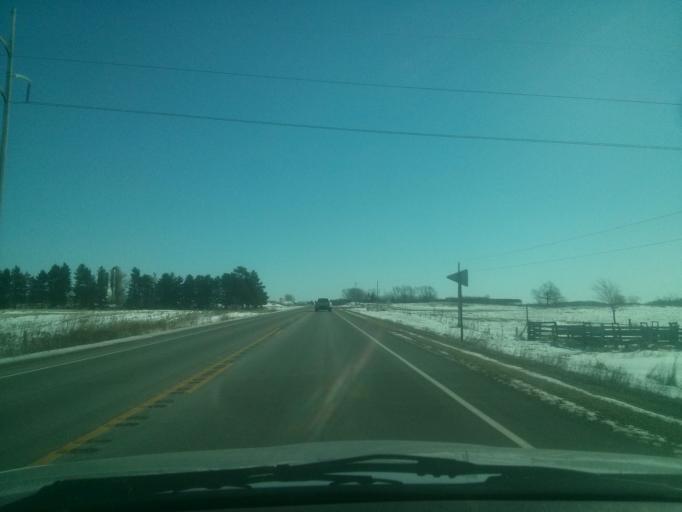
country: US
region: Wisconsin
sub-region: Polk County
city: Clear Lake
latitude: 45.1364
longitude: -92.3025
